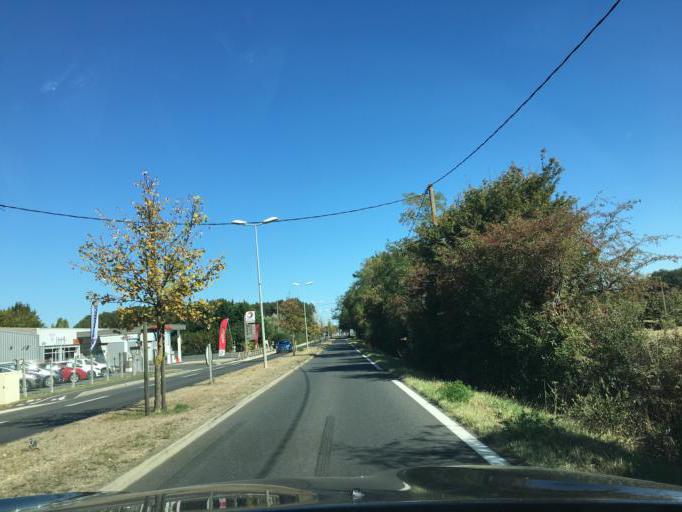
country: FR
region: Centre
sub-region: Departement d'Indre-et-Loire
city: Azay-le-Rideau
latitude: 47.2691
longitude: 0.4775
